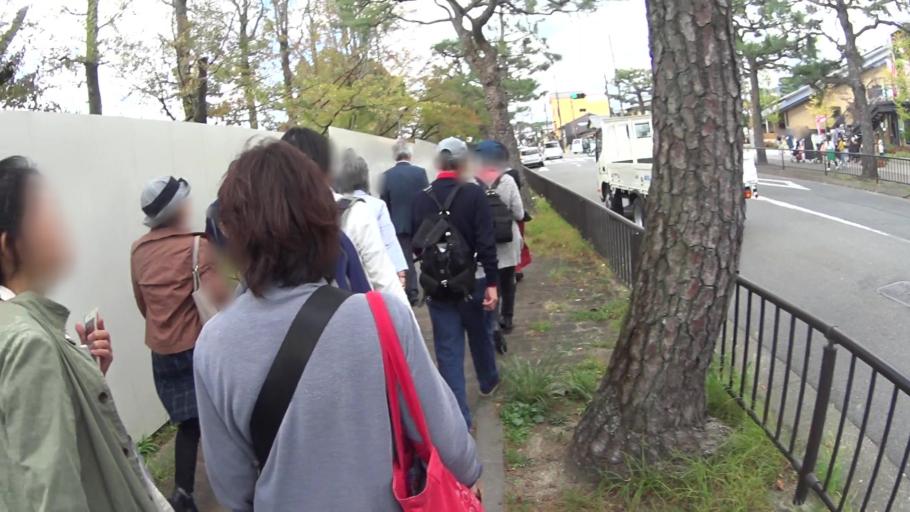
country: JP
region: Kyoto
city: Kyoto
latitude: 35.0131
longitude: 135.7847
